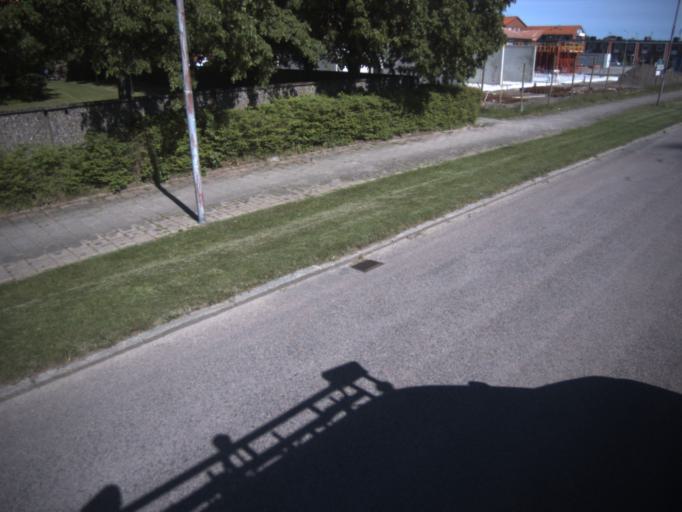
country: SE
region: Skane
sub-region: Helsingborg
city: Rydeback
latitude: 56.0037
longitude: 12.7300
